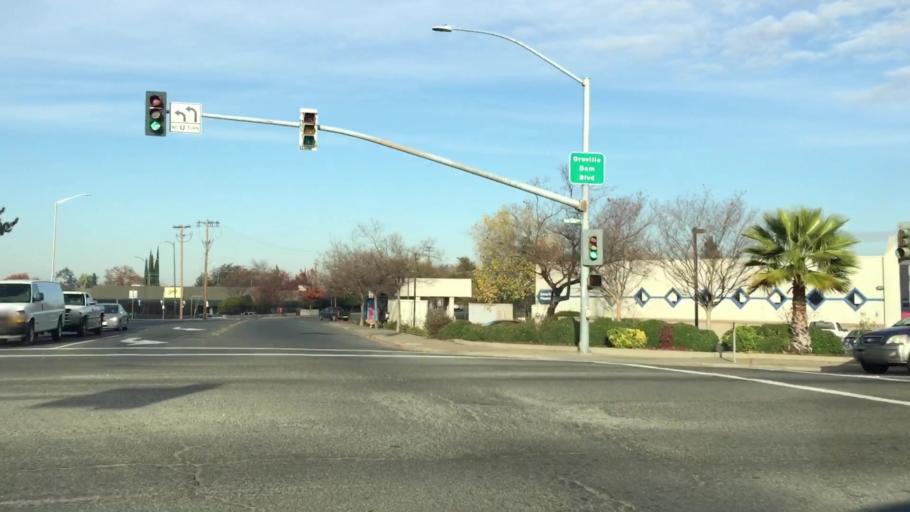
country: US
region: California
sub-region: Butte County
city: South Oroville
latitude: 39.5068
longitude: -121.5458
